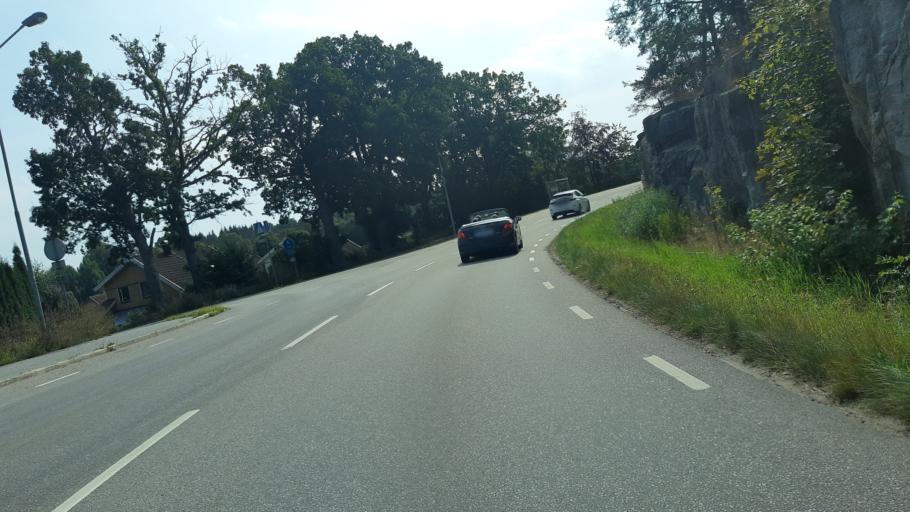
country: SE
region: Blekinge
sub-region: Karlskrona Kommun
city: Nattraby
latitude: 56.1945
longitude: 15.5356
